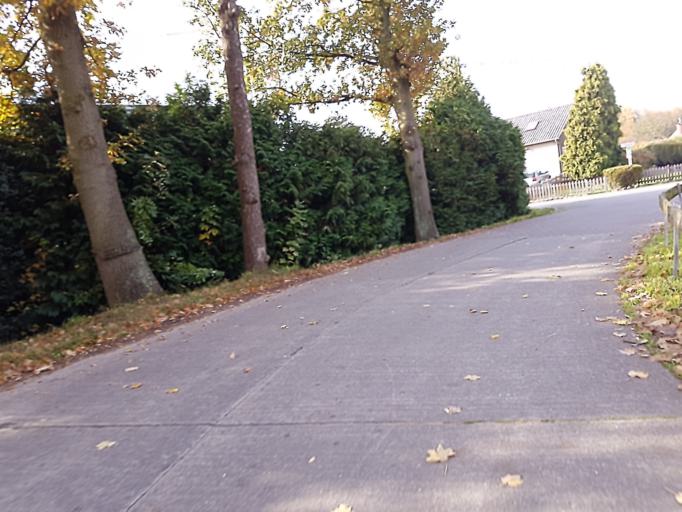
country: BE
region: Flanders
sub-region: Provincie Antwerpen
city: Sint-Katelijne-Waver
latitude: 51.0751
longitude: 4.5220
